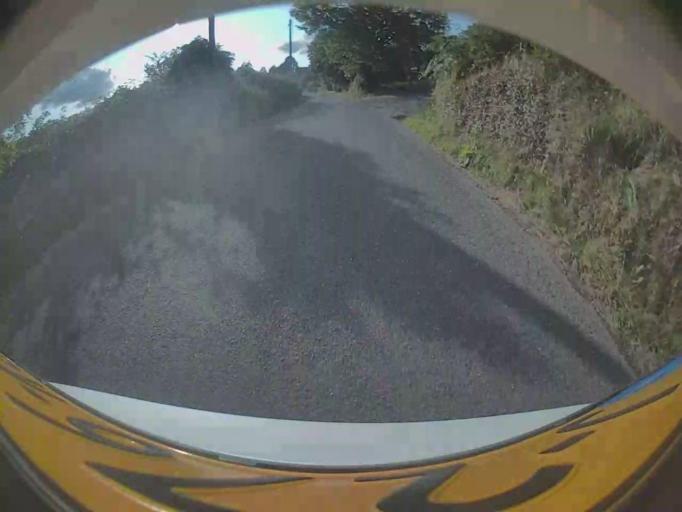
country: IE
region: Leinster
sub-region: Wicklow
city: Enniskerry
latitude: 53.1865
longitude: -6.2147
